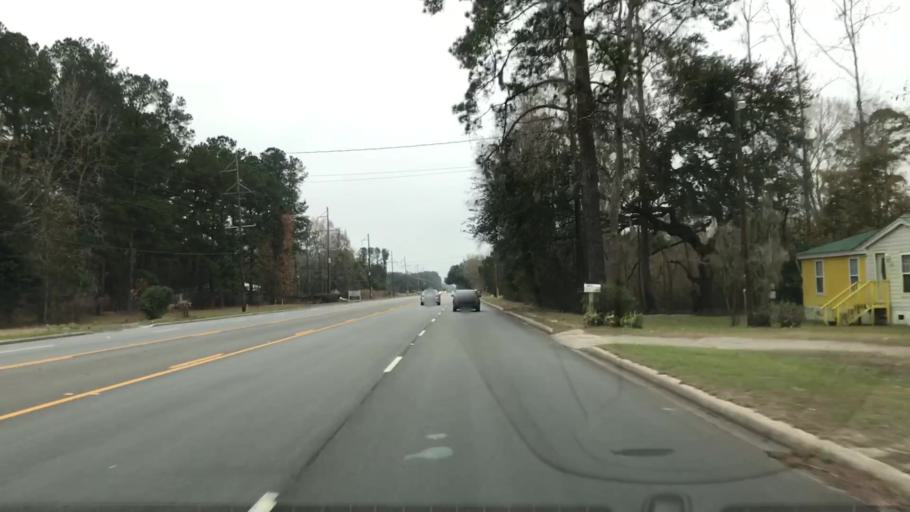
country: US
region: South Carolina
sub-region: Beaufort County
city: Laurel Bay
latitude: 32.5809
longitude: -80.7432
